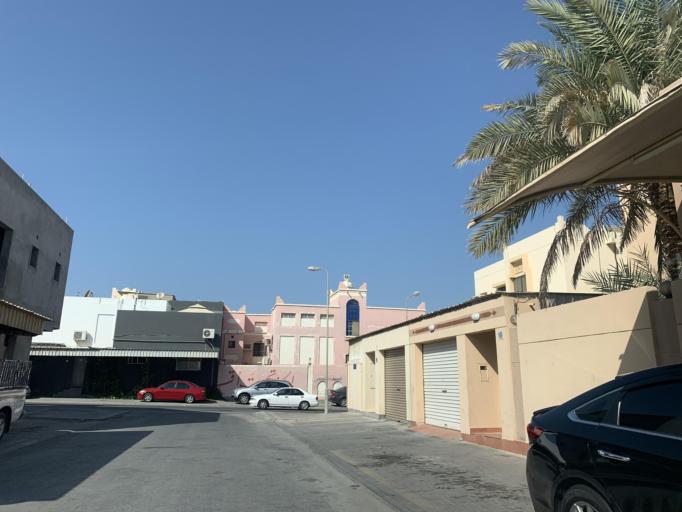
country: BH
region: Central Governorate
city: Madinat Hamad
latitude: 26.1262
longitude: 50.4804
